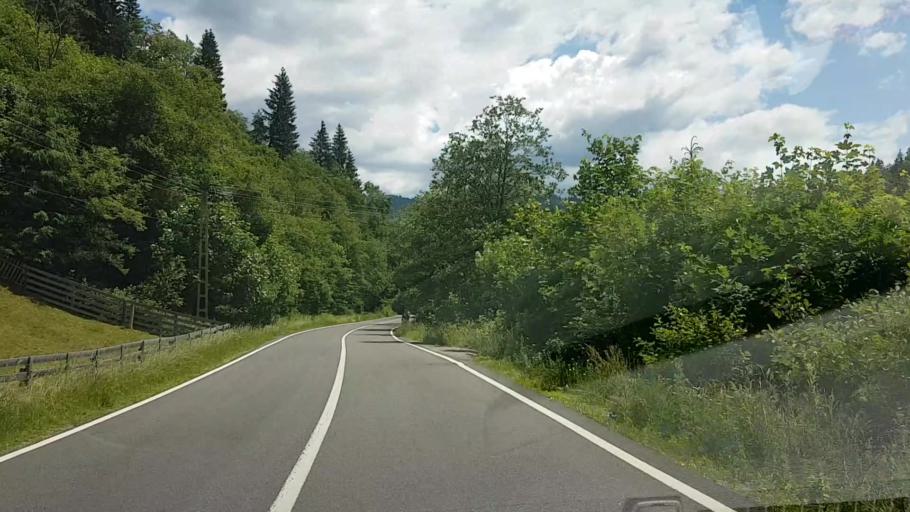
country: RO
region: Suceava
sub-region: Comuna Crucea
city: Crucea
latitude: 47.3940
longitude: 25.5663
